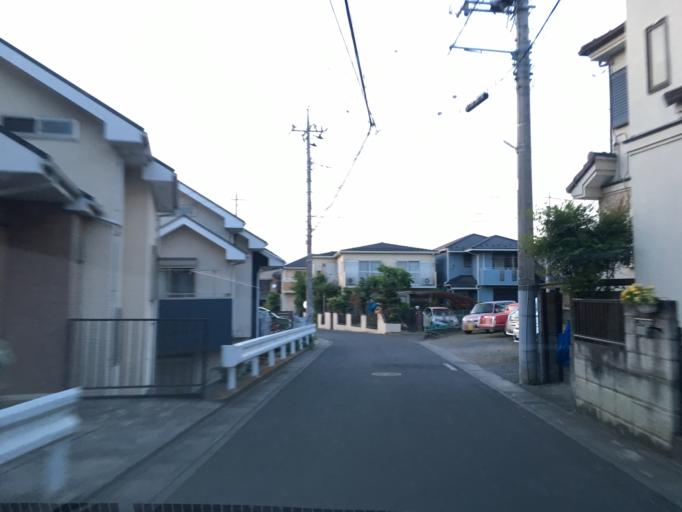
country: JP
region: Saitama
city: Sayama
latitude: 35.8436
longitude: 139.3766
